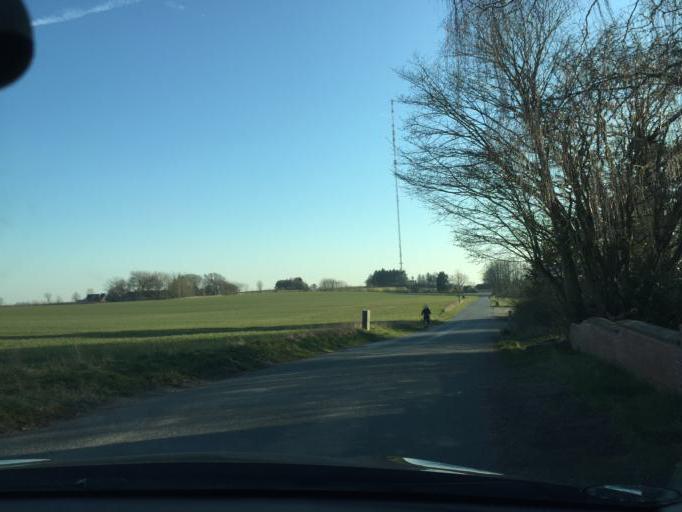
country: DK
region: South Denmark
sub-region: Faaborg-Midtfyn Kommune
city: Arslev
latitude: 55.2887
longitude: 10.4773
